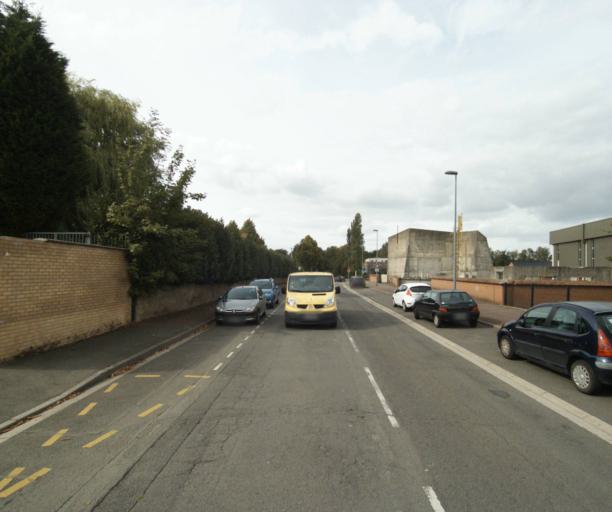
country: FR
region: Nord-Pas-de-Calais
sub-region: Departement du Nord
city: Lomme
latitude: 50.6502
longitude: 2.9970
